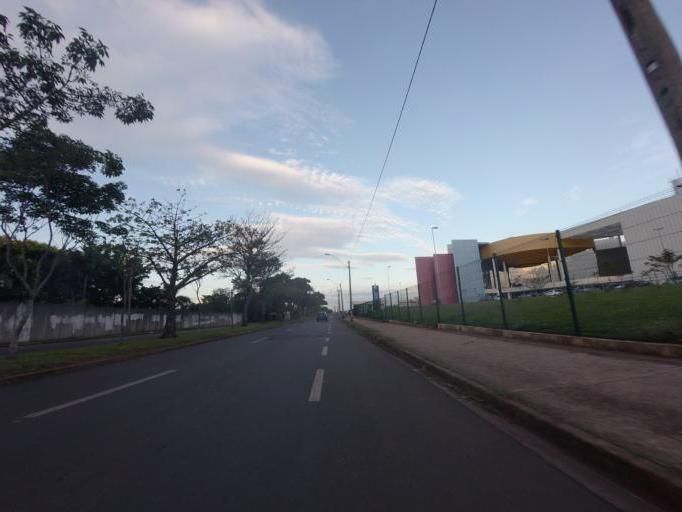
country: BR
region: Sao Paulo
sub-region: Piracicaba
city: Piracicaba
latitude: -22.7610
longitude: -47.5853
